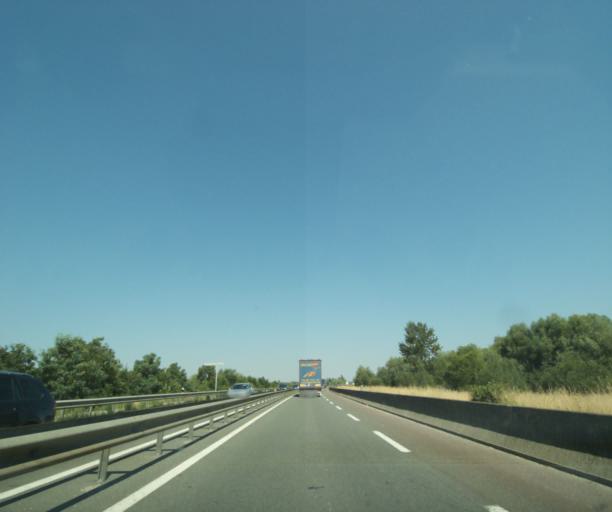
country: FR
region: Champagne-Ardenne
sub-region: Departement de la Haute-Marne
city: Saint-Dizier
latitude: 48.6293
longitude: 4.9294
